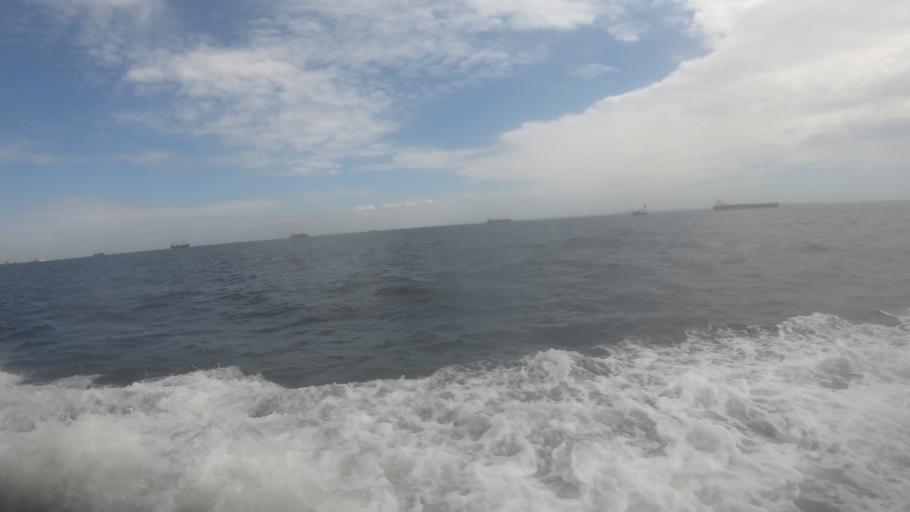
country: JP
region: Kanagawa
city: Yokohama
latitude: 35.4291
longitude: 139.6909
